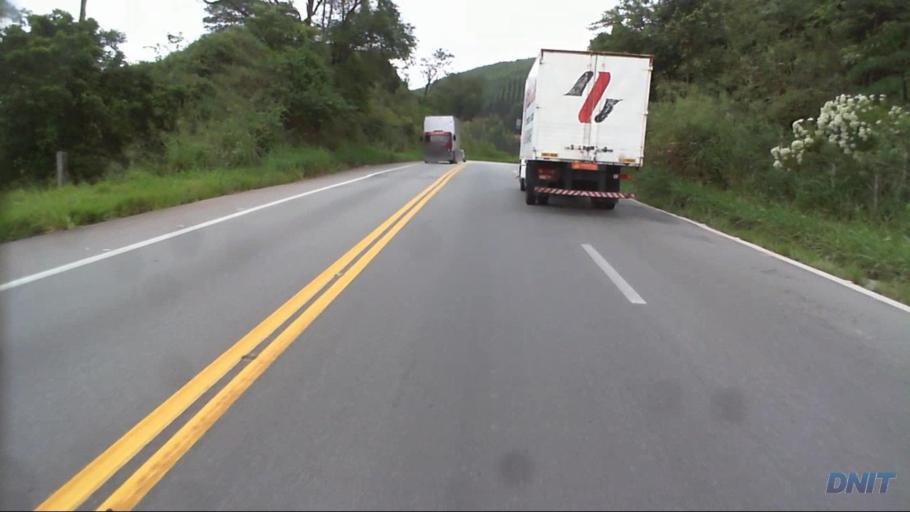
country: BR
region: Minas Gerais
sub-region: Nova Era
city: Nova Era
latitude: -19.6674
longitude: -42.9658
